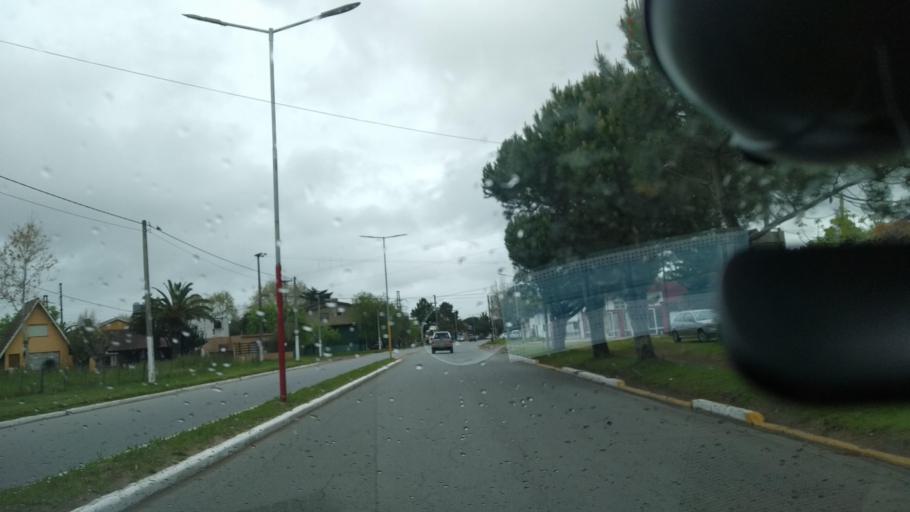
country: AR
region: Buenos Aires
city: San Clemente del Tuyu
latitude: -36.3799
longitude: -56.7211
